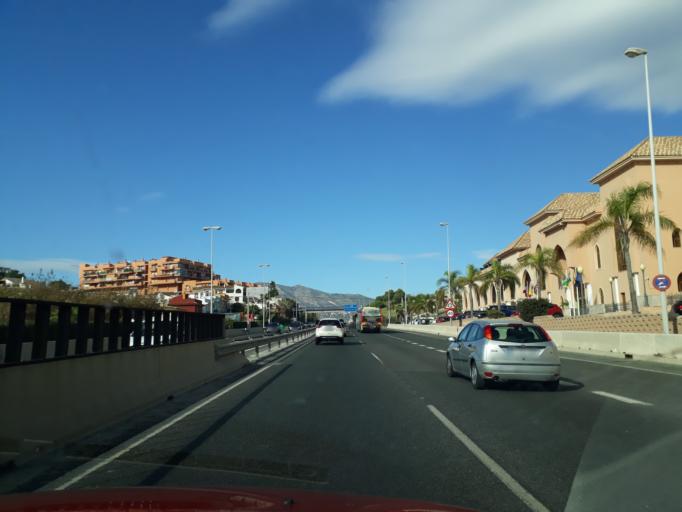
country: ES
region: Andalusia
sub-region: Provincia de Malaga
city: Fuengirola
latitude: 36.5209
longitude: -4.6301
